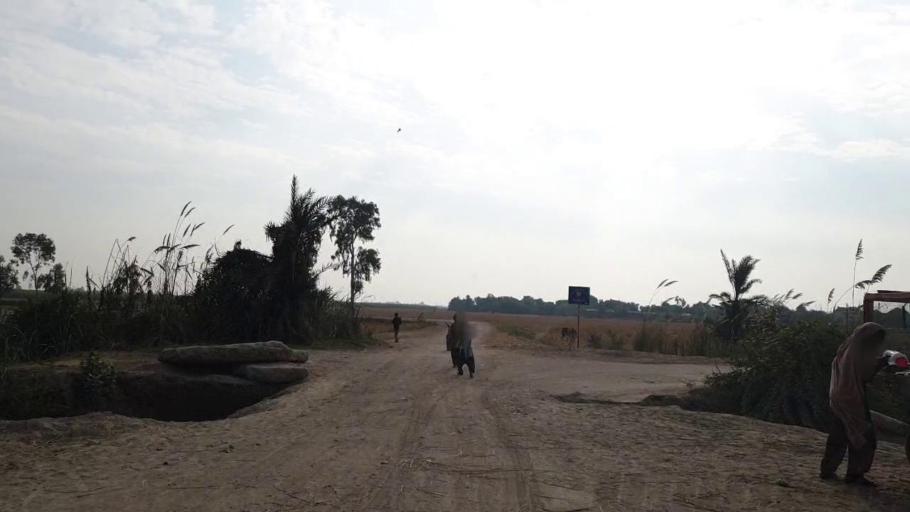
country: PK
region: Sindh
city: Tando Muhammad Khan
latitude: 25.0371
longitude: 68.4361
